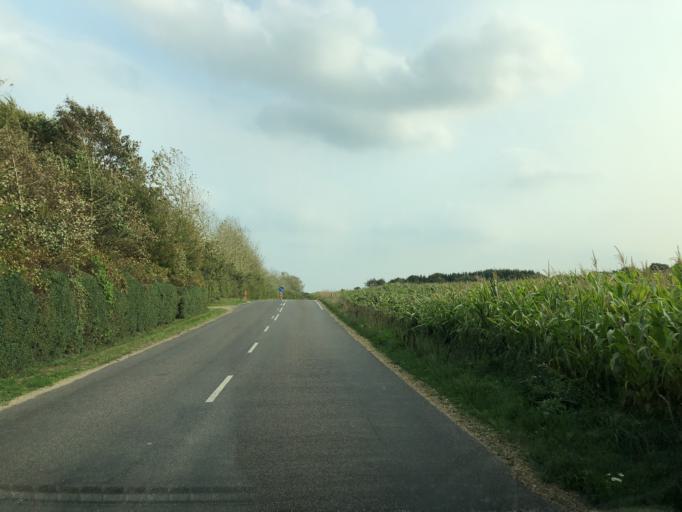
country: DK
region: Central Jutland
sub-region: Ringkobing-Skjern Kommune
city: Videbaek
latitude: 56.0840
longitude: 8.7035
